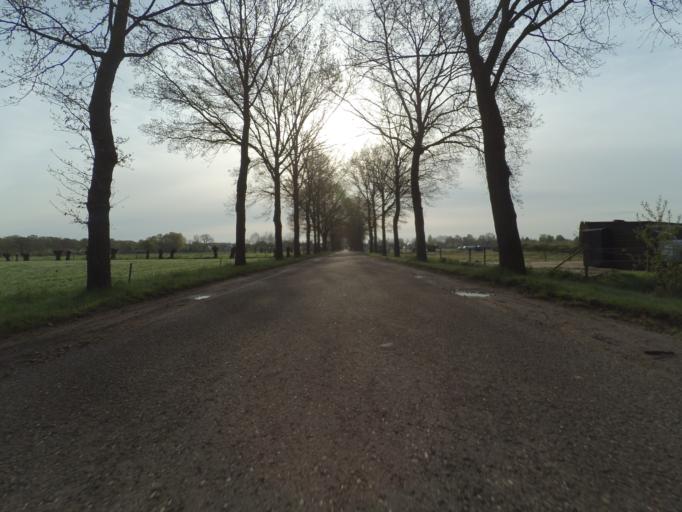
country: NL
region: Utrecht
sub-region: Gemeente Woudenberg
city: Woudenberg
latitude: 52.0859
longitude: 5.3977
